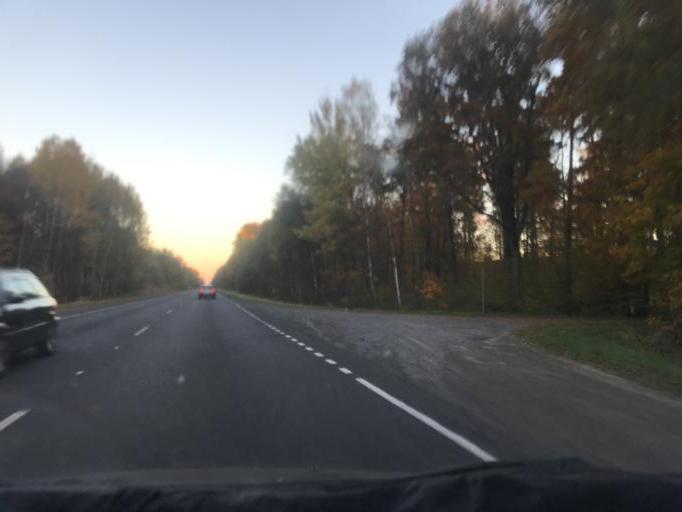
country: BY
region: Gomel
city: Mazyr
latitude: 52.1895
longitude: 29.1300
